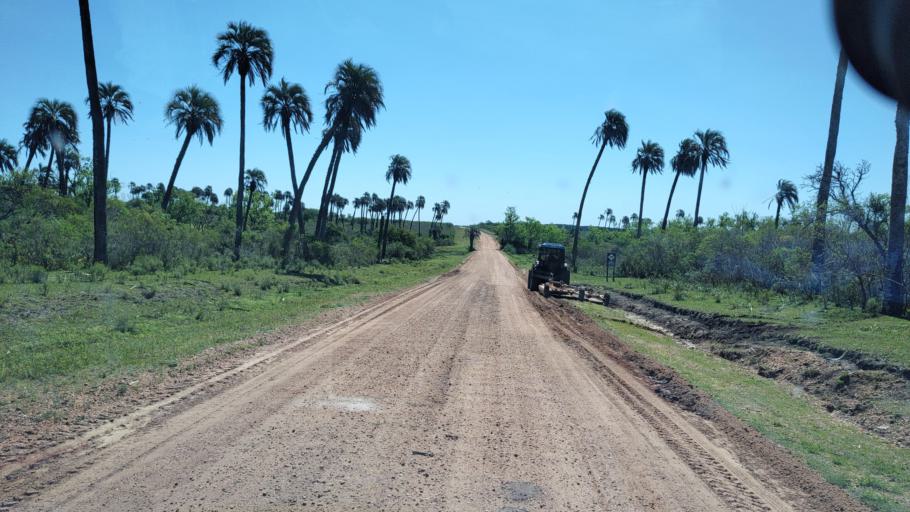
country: AR
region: Entre Rios
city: Ubajay
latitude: -31.8695
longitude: -58.2440
